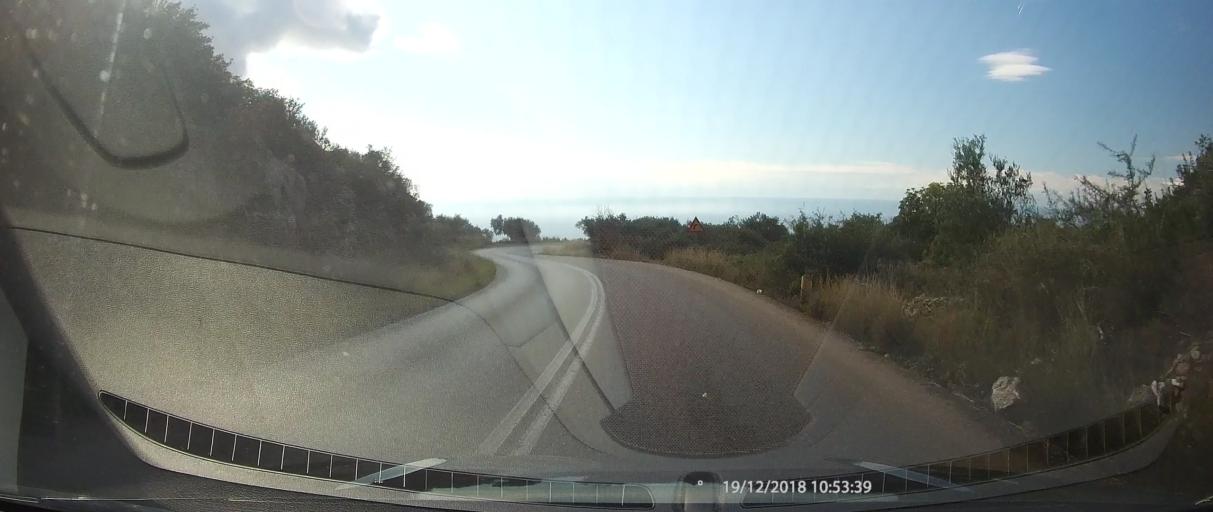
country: GR
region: Peloponnese
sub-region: Nomos Messinias
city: Kardamyli
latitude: 36.9098
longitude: 22.2330
